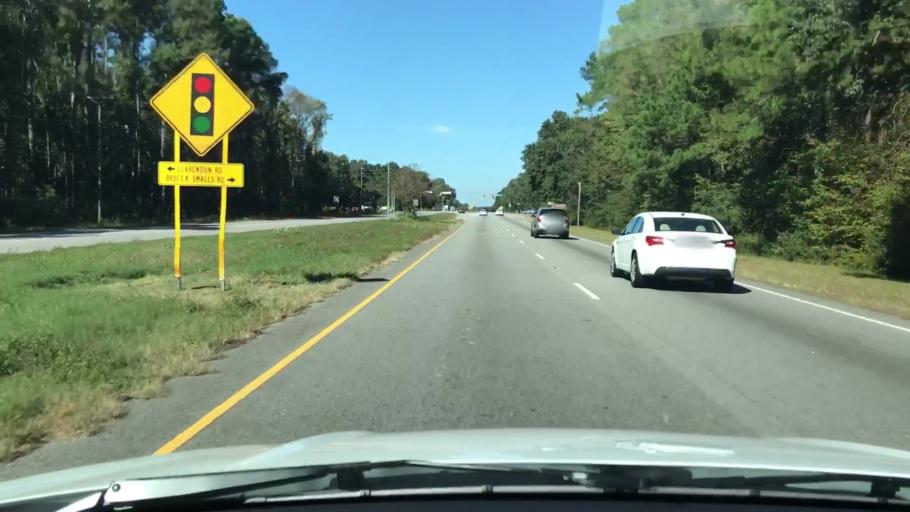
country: US
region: South Carolina
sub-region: Beaufort County
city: Burton
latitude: 32.4909
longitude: -80.7415
